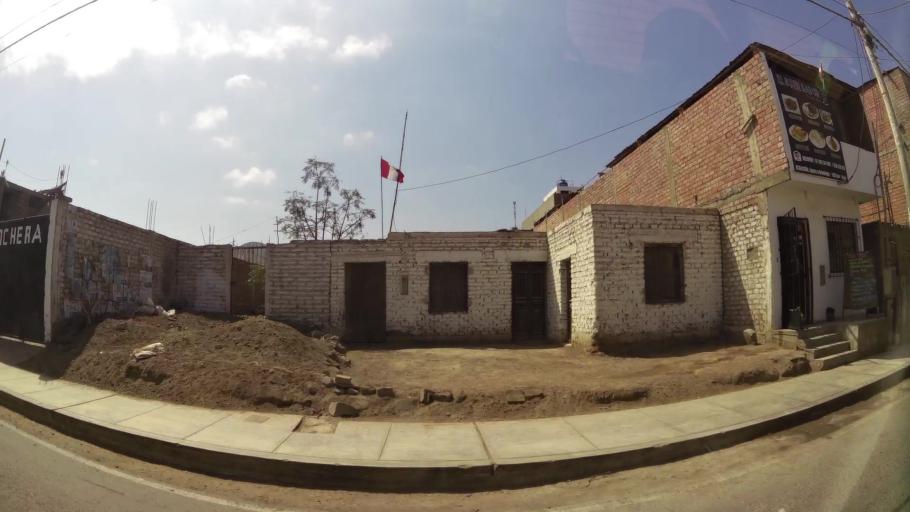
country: PE
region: Lima
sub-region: Provincia de Canete
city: Mala
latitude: -12.6580
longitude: -76.6306
